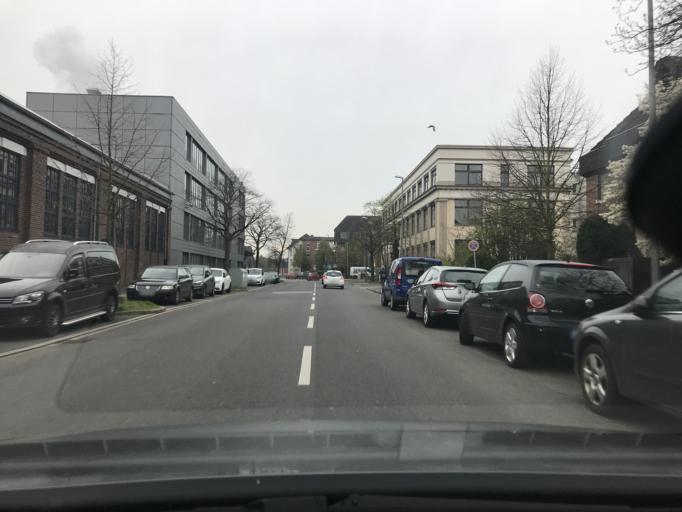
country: DE
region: North Rhine-Westphalia
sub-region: Regierungsbezirk Dusseldorf
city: Krefeld
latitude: 51.3581
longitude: 6.6418
